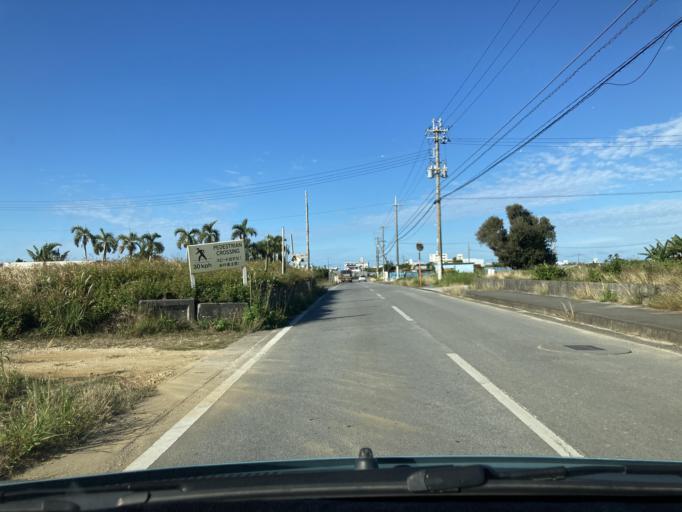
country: JP
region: Okinawa
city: Chatan
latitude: 26.3706
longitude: 127.7429
